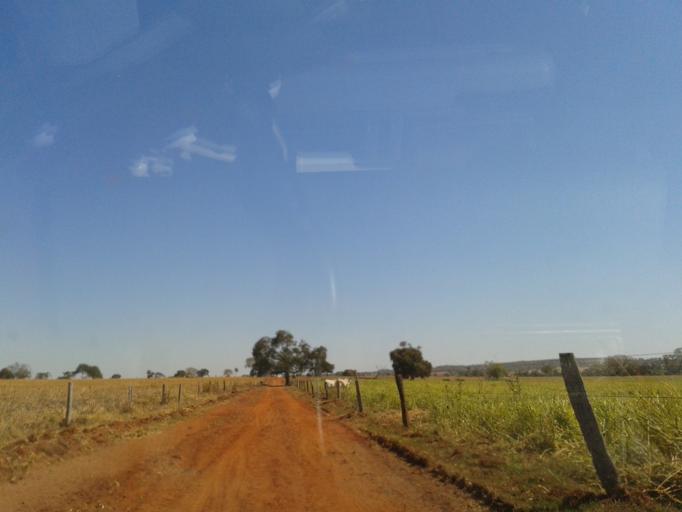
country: BR
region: Minas Gerais
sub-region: Santa Vitoria
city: Santa Vitoria
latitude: -19.0804
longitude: -50.0686
